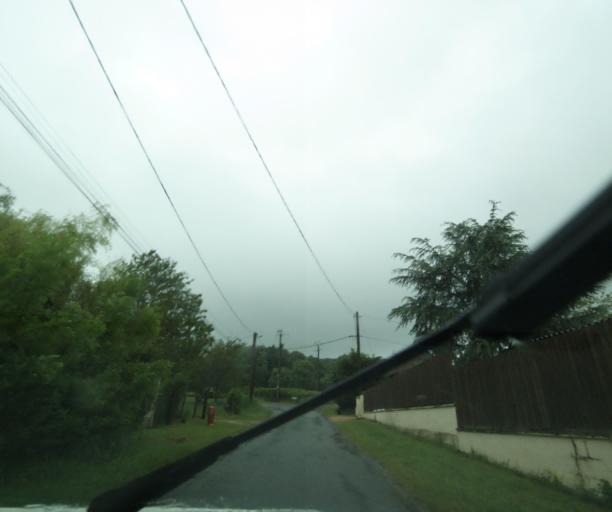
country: FR
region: Bourgogne
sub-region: Departement de Saone-et-Loire
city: Palinges
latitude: 46.5255
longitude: 4.2898
